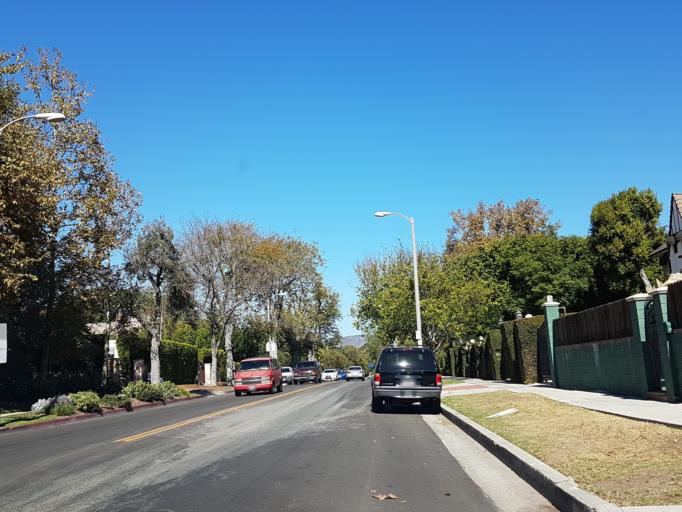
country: US
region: California
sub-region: Los Angeles County
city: Hollywood
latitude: 34.0716
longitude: -118.3273
